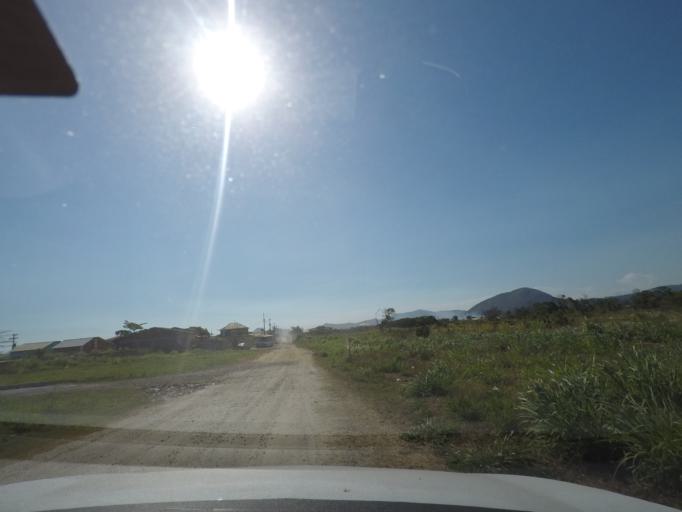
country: BR
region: Rio de Janeiro
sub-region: Marica
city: Marica
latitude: -22.9643
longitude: -42.9215
